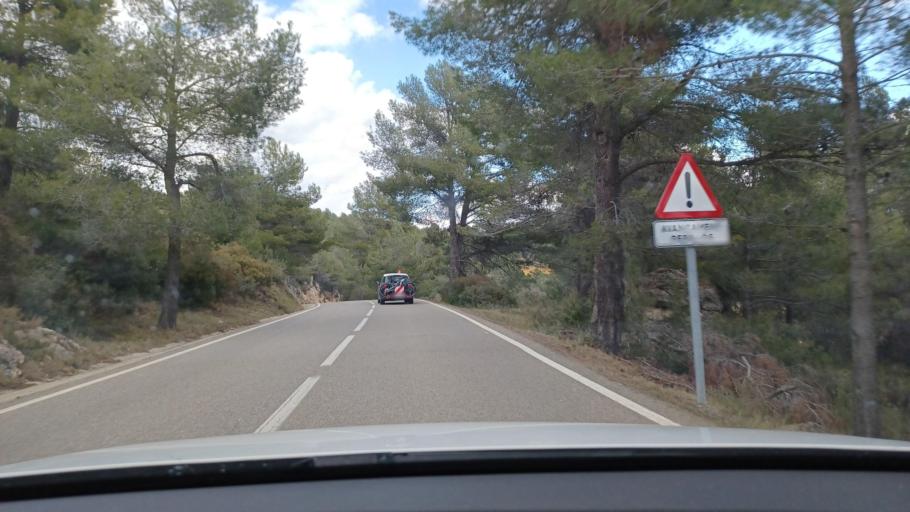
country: ES
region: Catalonia
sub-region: Provincia de Tarragona
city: la Morera de Montsant
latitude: 41.2681
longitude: 0.8612
